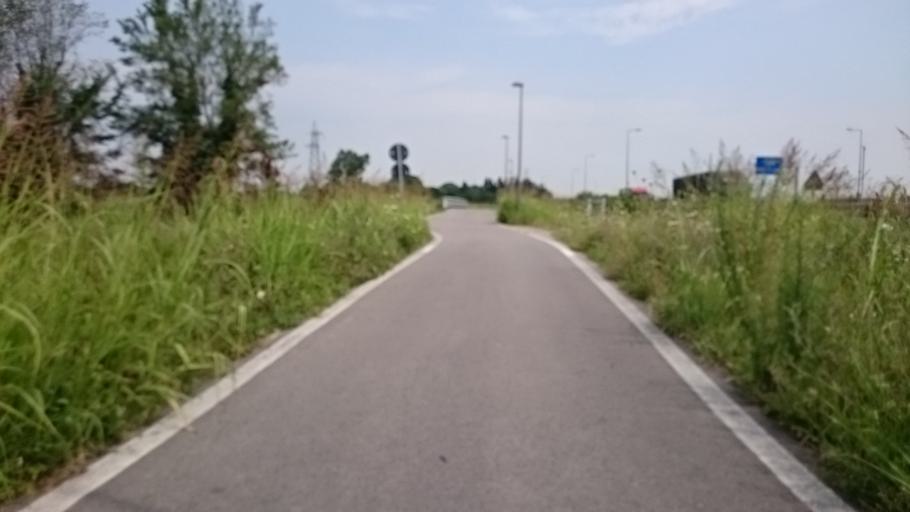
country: IT
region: Veneto
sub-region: Provincia di Venezia
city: Mestre
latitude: 45.4581
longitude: 12.2090
